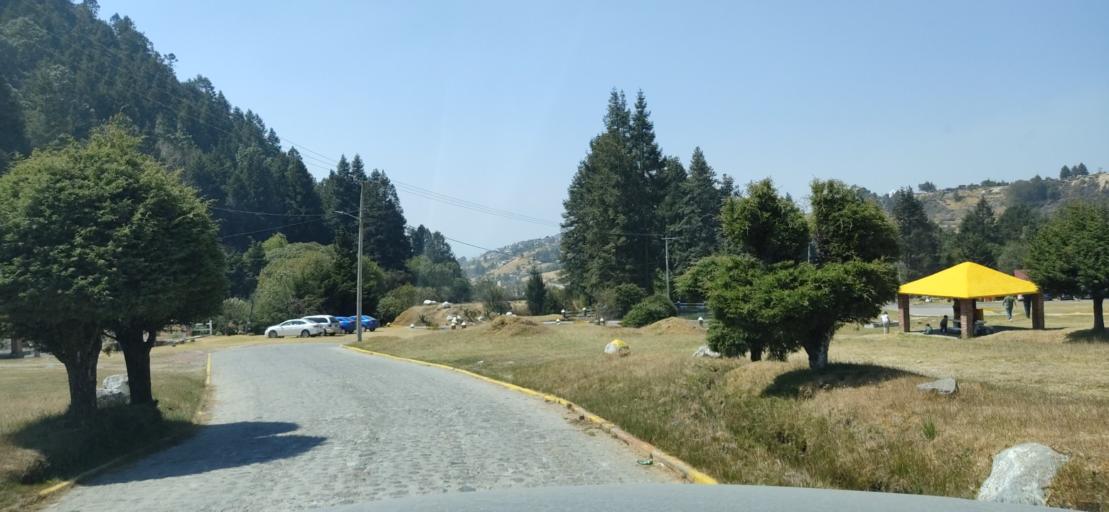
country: MX
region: Mexico
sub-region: Ocoyoacac
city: San Jeronimo Acazulco
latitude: 19.2418
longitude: -99.3791
